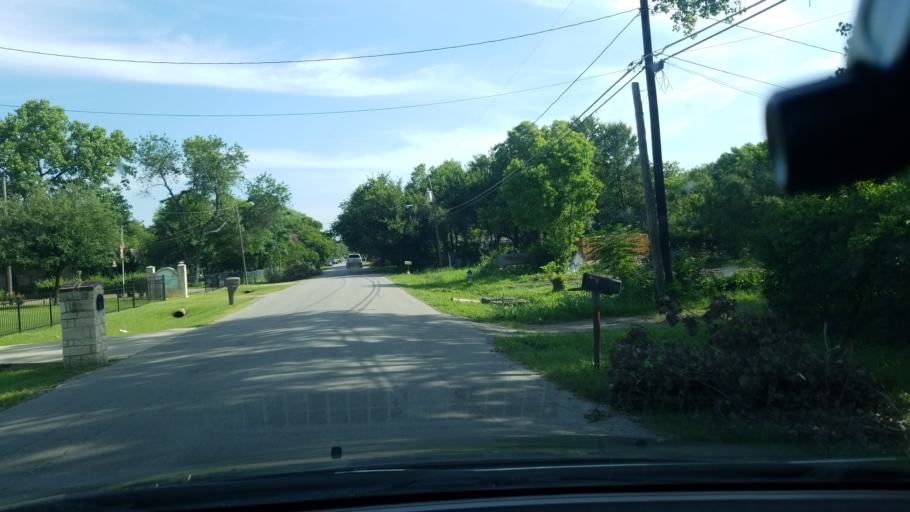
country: US
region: Texas
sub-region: Dallas County
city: Balch Springs
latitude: 32.7139
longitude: -96.6388
